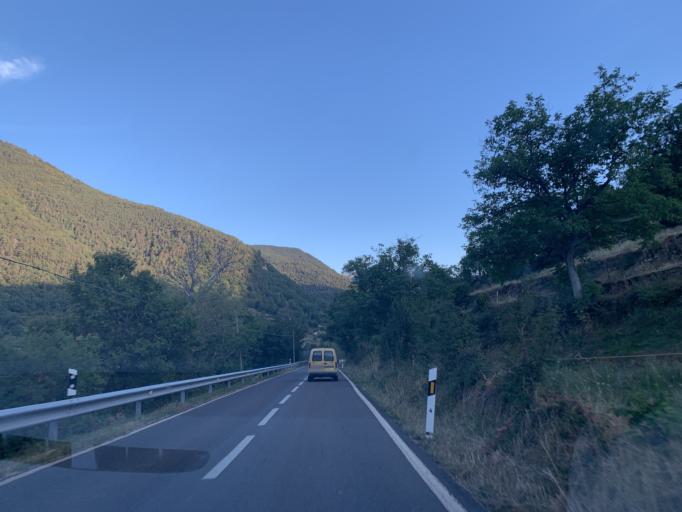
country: ES
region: Aragon
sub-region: Provincia de Huesca
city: Broto
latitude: 42.6100
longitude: -0.1238
